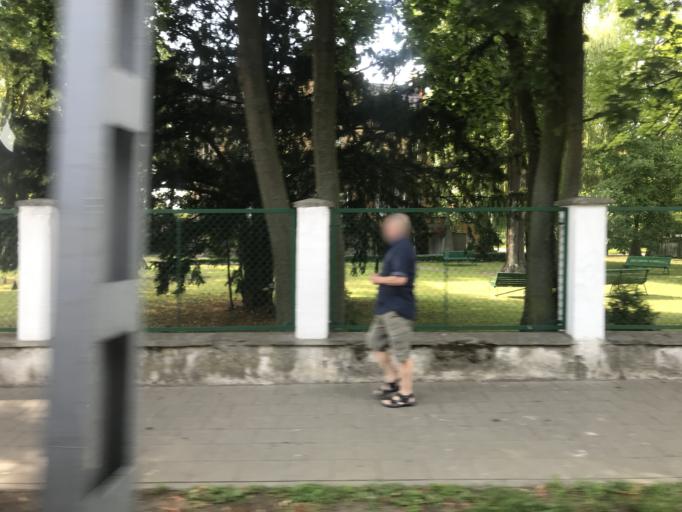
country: PL
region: Pomeranian Voivodeship
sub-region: Gdansk
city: Gdansk
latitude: 54.4049
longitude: 18.6348
